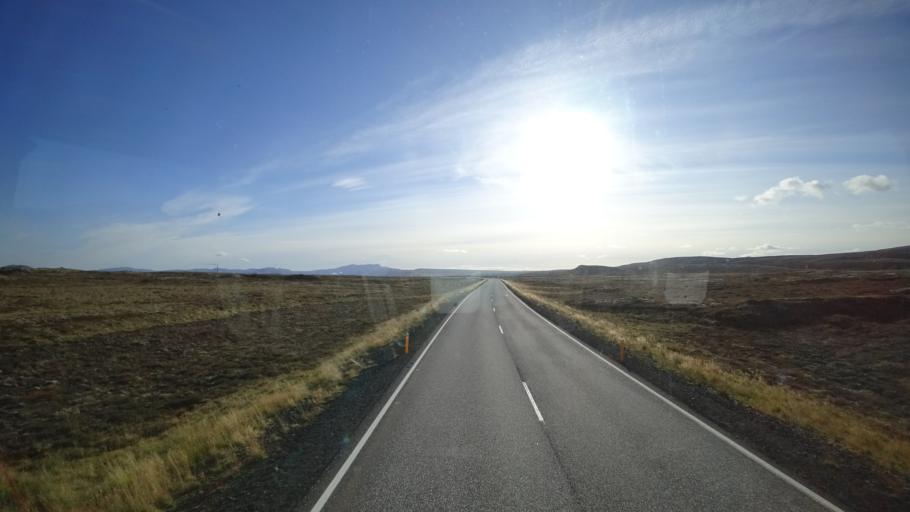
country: IS
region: South
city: Hveragerdi
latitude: 64.2640
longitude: -21.1295
